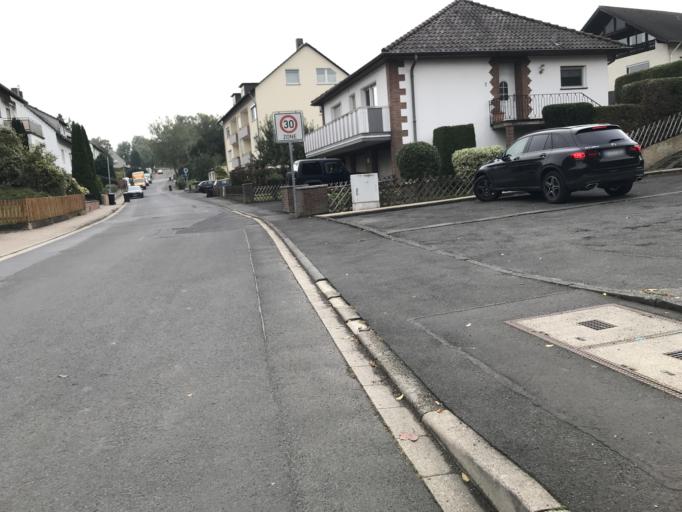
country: DE
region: Hesse
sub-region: Regierungsbezirk Kassel
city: Guxhagen
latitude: 51.2102
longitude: 9.4437
